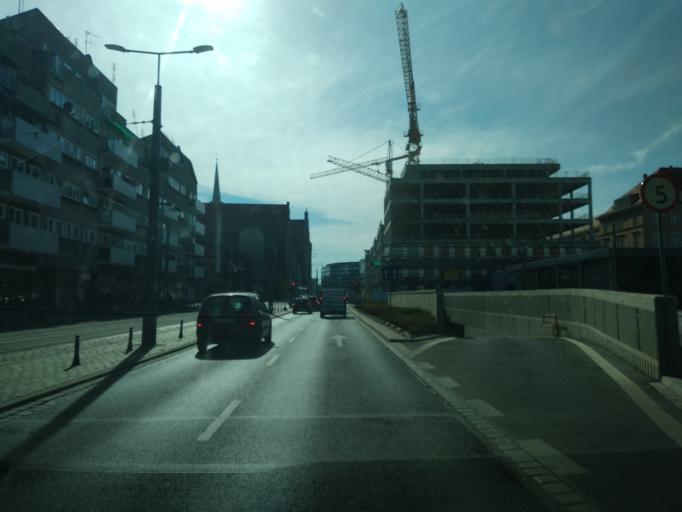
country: PL
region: Lower Silesian Voivodeship
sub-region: Powiat wroclawski
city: Wroclaw
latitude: 51.1115
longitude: 17.0392
